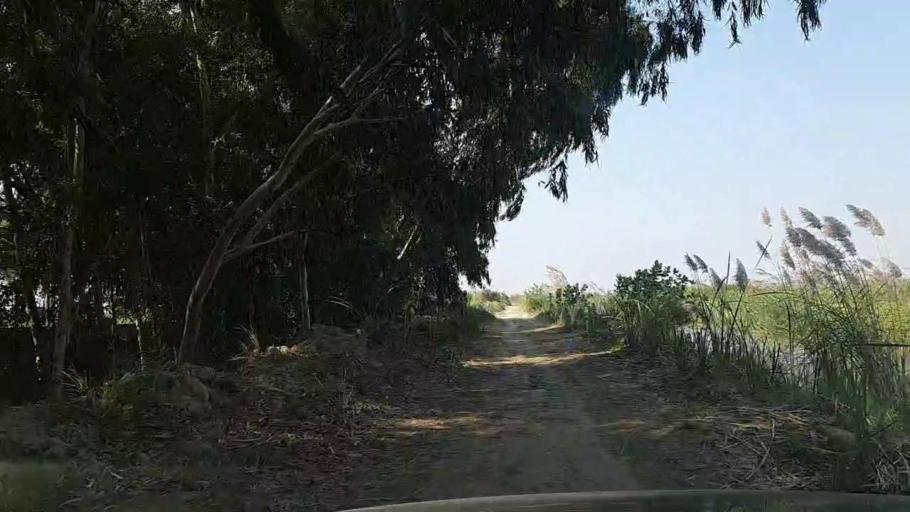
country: PK
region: Sindh
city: Gharo
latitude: 24.7220
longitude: 67.6729
